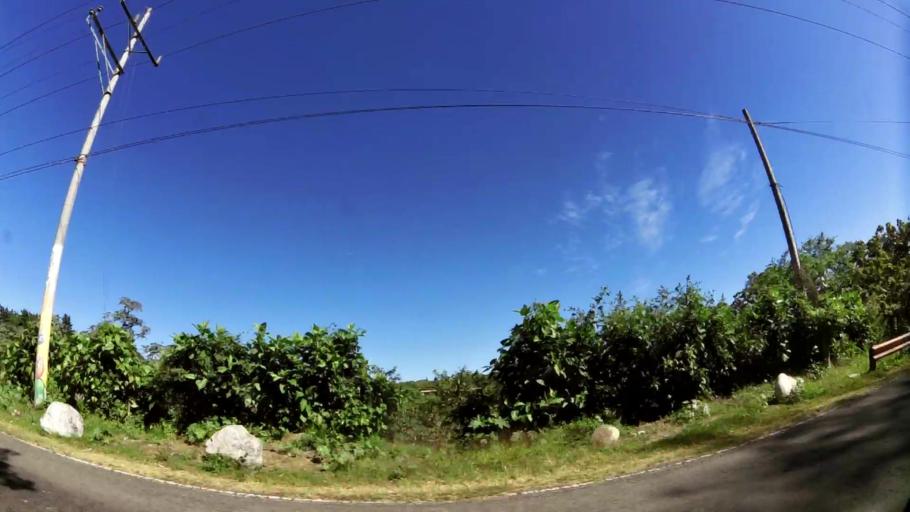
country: SV
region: Ahuachapan
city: Concepcion de Ataco
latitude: 13.8652
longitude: -89.8470
